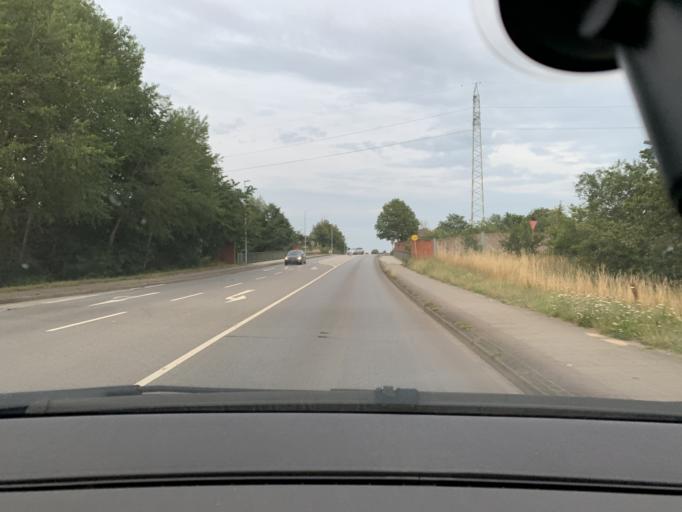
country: DE
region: Schleswig-Holstein
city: Mildstedt
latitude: 54.4725
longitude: 9.0794
